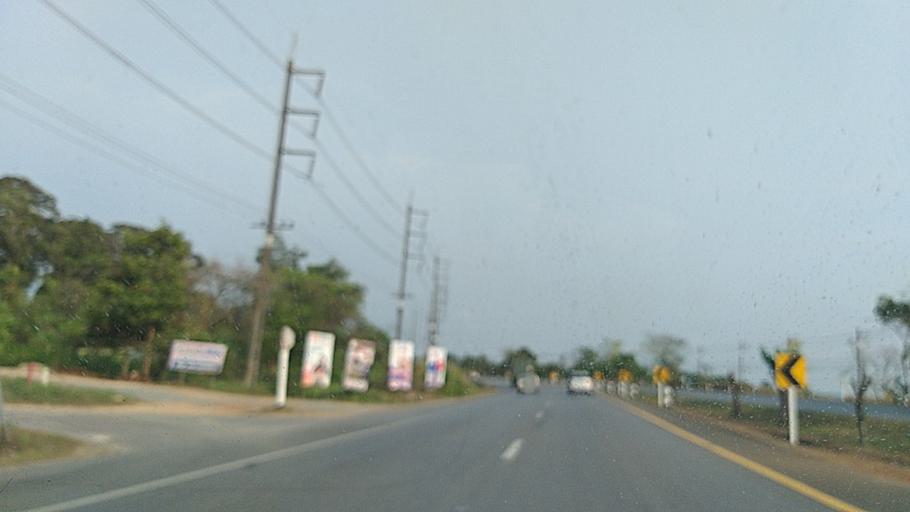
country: TH
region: Chanthaburi
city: Khlung
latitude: 12.4488
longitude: 102.2873
